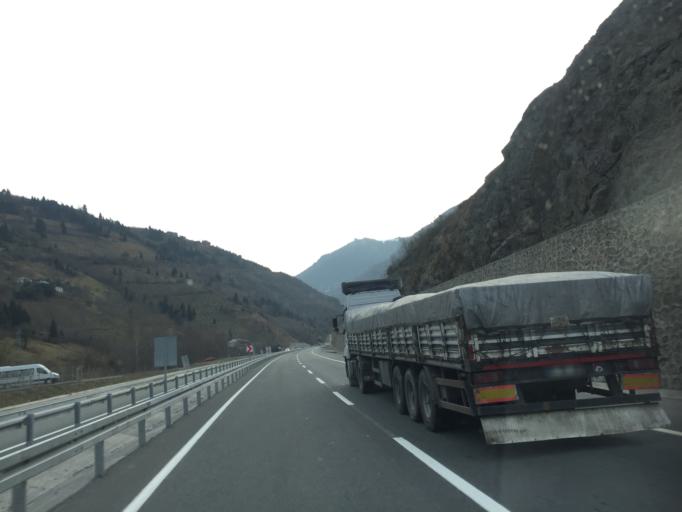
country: TR
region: Trabzon
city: Macka
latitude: 40.7902
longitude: 39.5802
